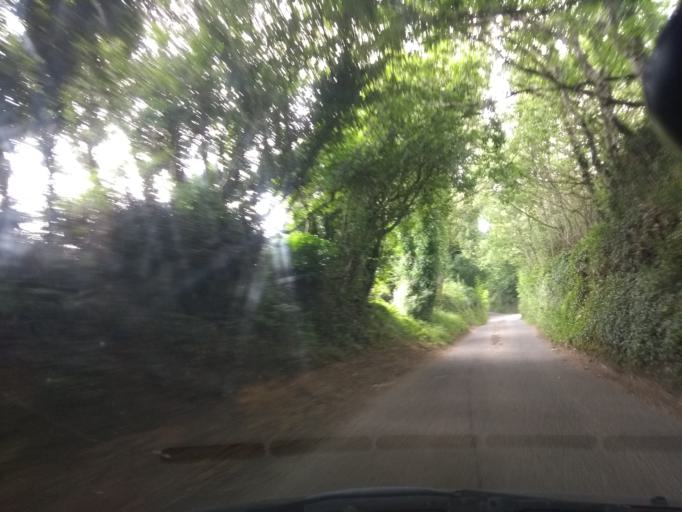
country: GB
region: England
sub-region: Devon
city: Modbury
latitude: 50.3062
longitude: -3.8541
